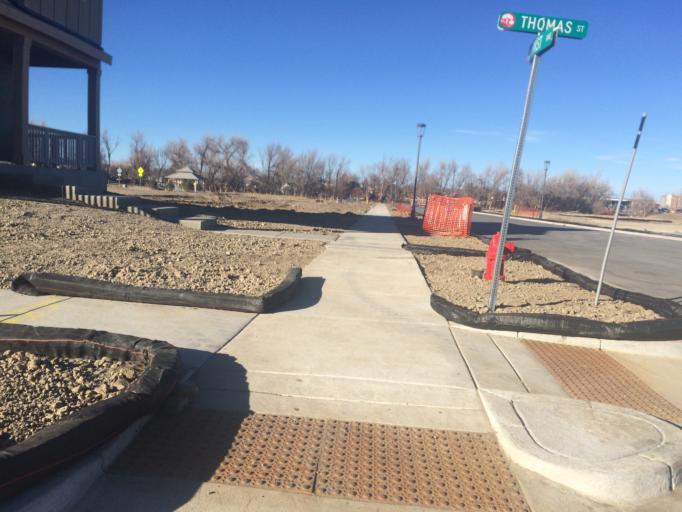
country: US
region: Colorado
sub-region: Boulder County
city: Superior
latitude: 39.9505
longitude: -105.1669
